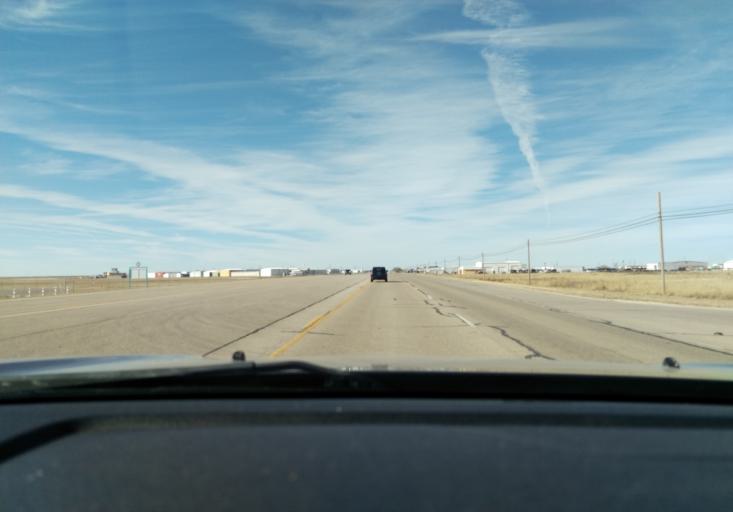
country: US
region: New Mexico
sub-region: Lea County
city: Hobbs
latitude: 32.6967
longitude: -103.2035
